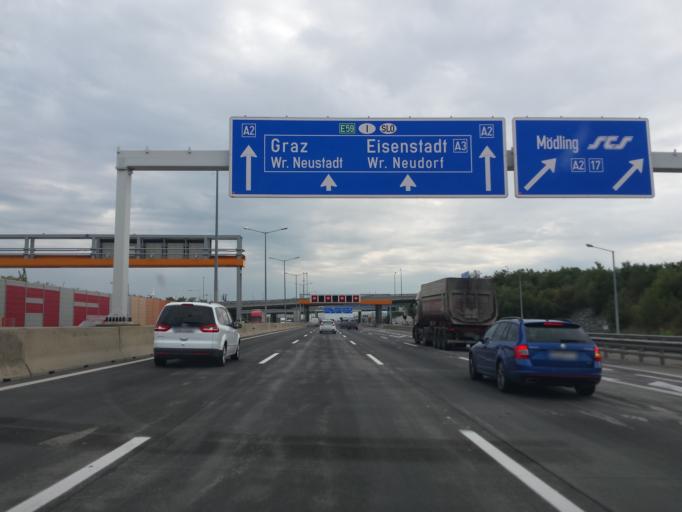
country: AT
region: Lower Austria
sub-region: Politischer Bezirk Modling
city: Vosendorf
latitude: 48.1221
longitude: 16.3253
